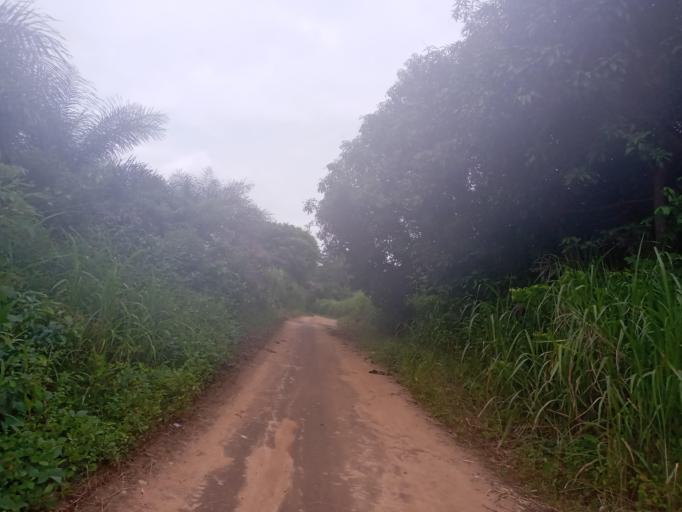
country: SL
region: Northern Province
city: Bumbuna
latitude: 8.9573
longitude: -11.7593
